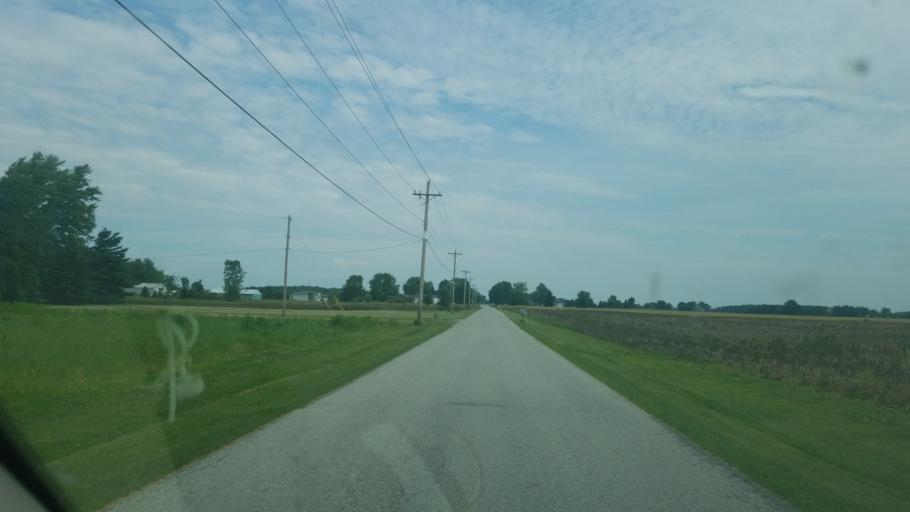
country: US
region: Ohio
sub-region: Seneca County
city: Fostoria
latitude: 41.0617
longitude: -83.4633
